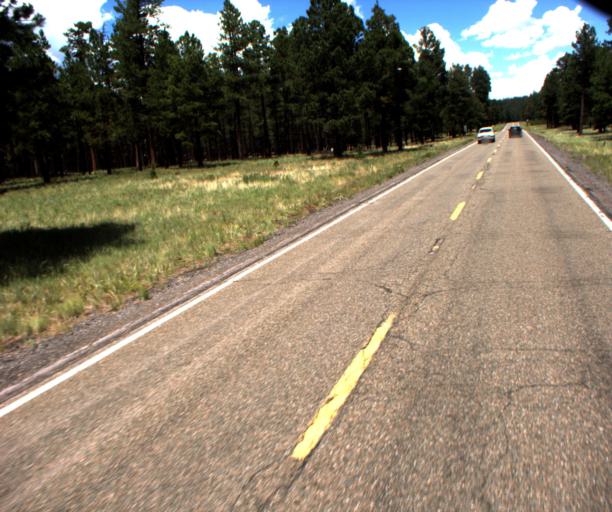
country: US
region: Arizona
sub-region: Coconino County
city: Parks
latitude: 35.3691
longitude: -111.7907
